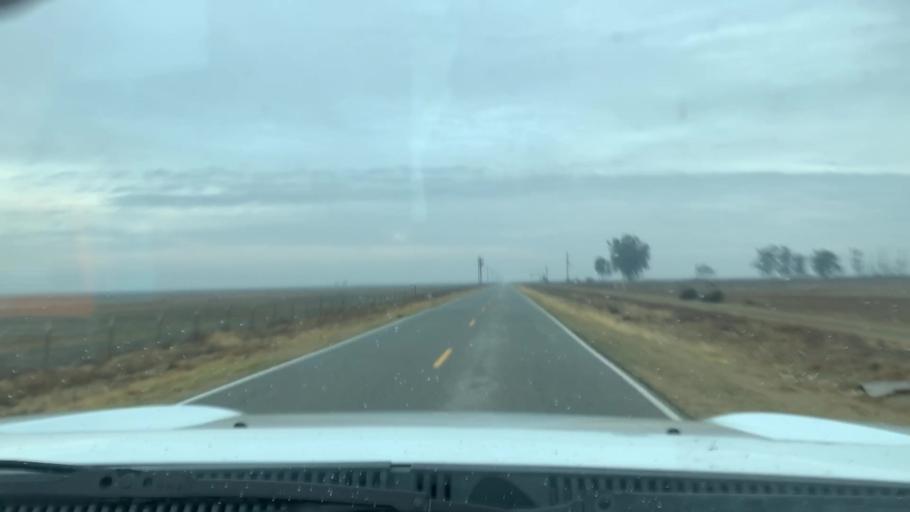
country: US
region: California
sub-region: Kern County
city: Lost Hills
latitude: 35.6640
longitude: -119.5799
